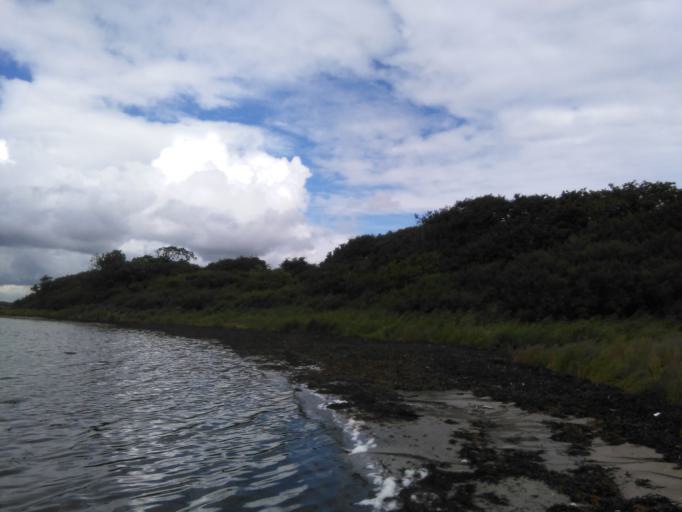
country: DK
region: Central Jutland
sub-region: Odder Kommune
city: Odder
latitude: 55.8585
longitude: 10.1405
